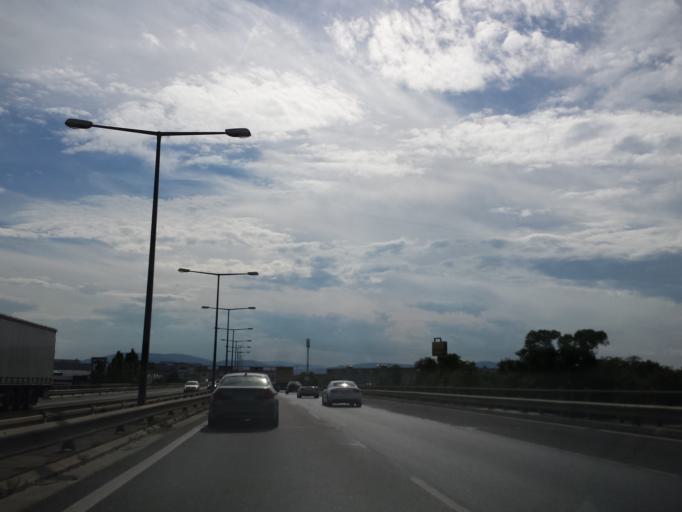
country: AT
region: Lower Austria
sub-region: Politischer Bezirk Modling
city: Vosendorf
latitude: 48.1498
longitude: 16.3436
